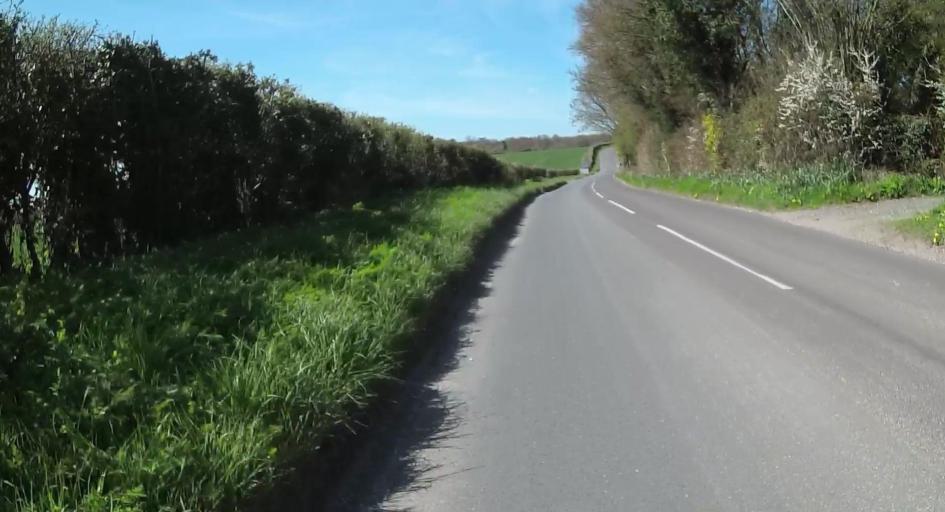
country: GB
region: England
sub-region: Hampshire
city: Winchester
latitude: 51.1064
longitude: -1.3804
